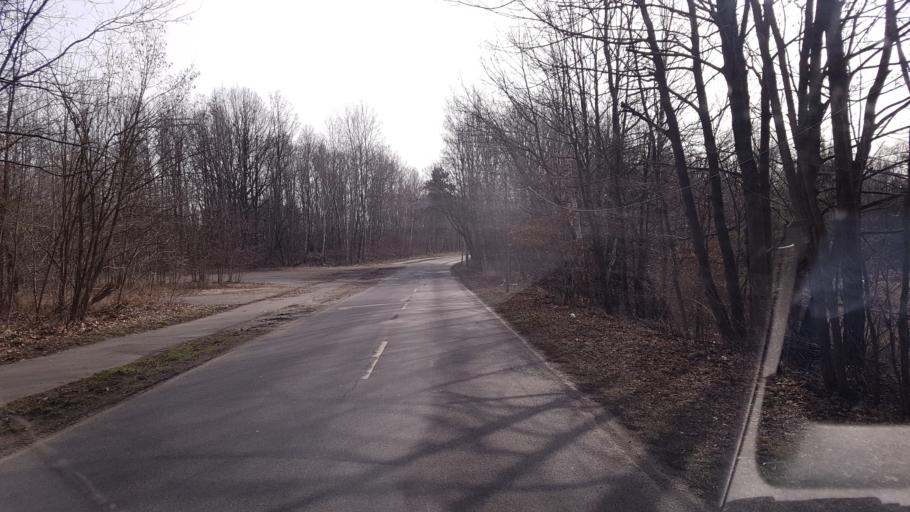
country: DE
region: Brandenburg
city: Schipkau
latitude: 51.5203
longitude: 13.8363
